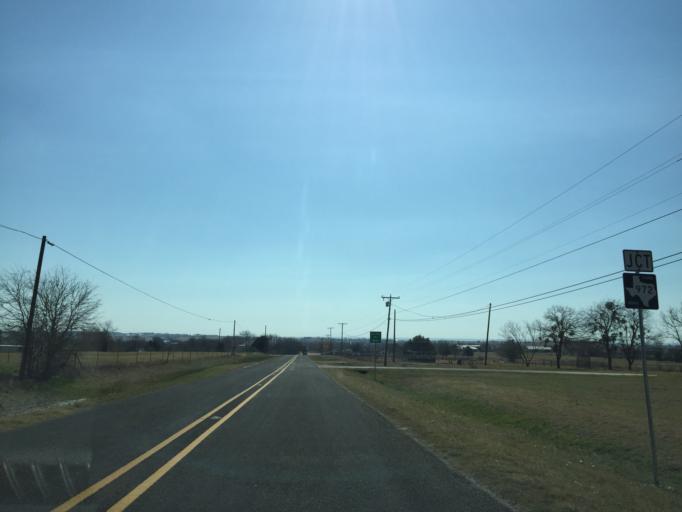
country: US
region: Texas
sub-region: Williamson County
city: Serenada
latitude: 30.7412
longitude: -97.5987
